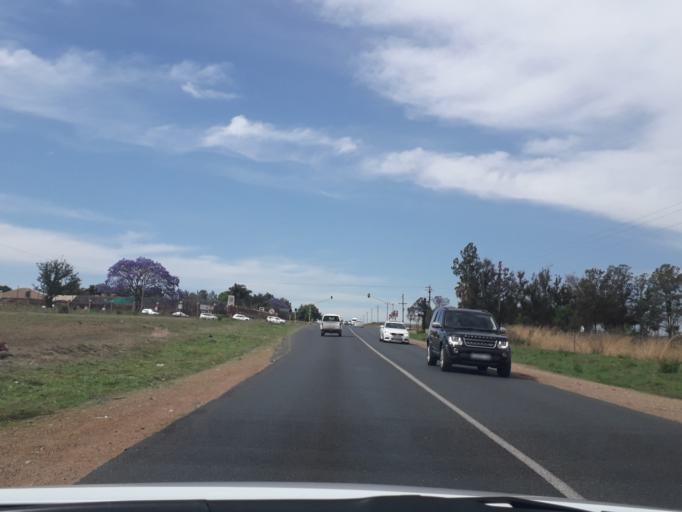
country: ZA
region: Gauteng
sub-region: City of Johannesburg Metropolitan Municipality
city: Diepsloot
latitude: -26.0023
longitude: 28.0417
